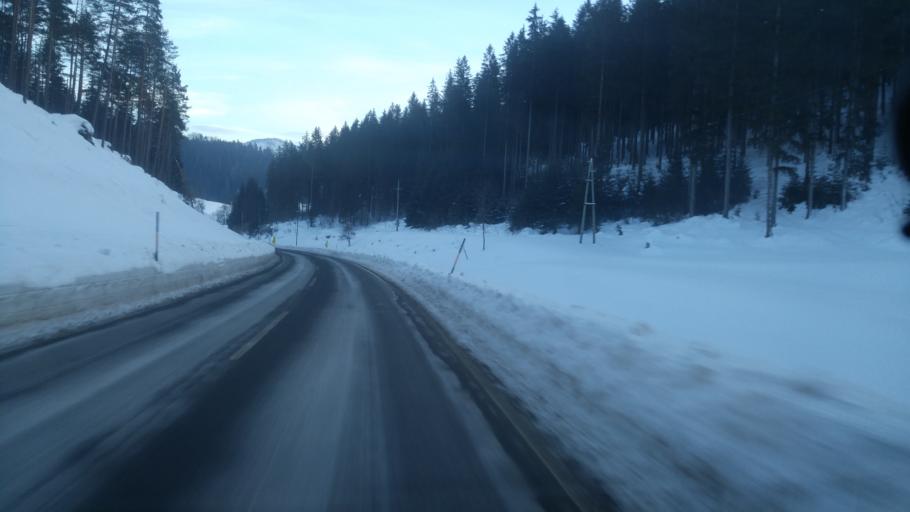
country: AT
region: Lower Austria
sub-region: Politischer Bezirk Wiener Neustadt
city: Rohr im Gebirge
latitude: 47.8714
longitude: 15.6982
